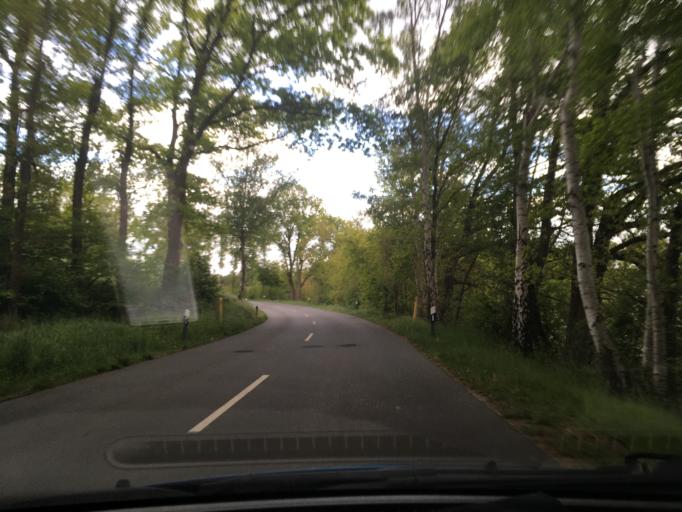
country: DE
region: Lower Saxony
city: Suderburg
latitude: 52.9143
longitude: 10.4700
